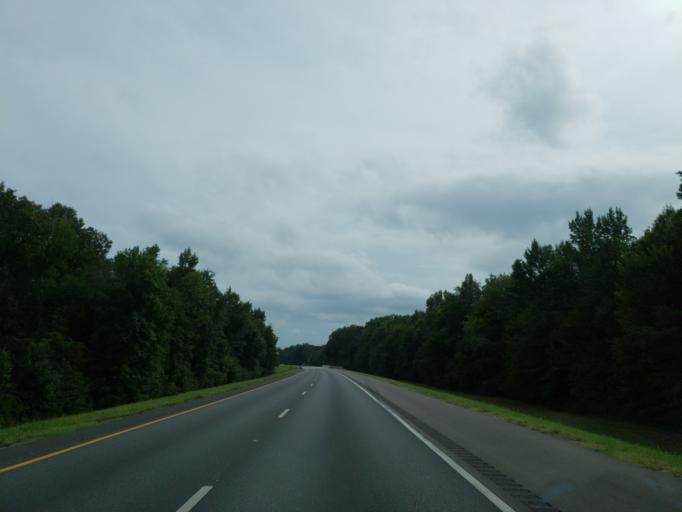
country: US
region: Alabama
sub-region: Tuscaloosa County
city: Tuscaloosa
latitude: 33.1280
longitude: -87.6455
